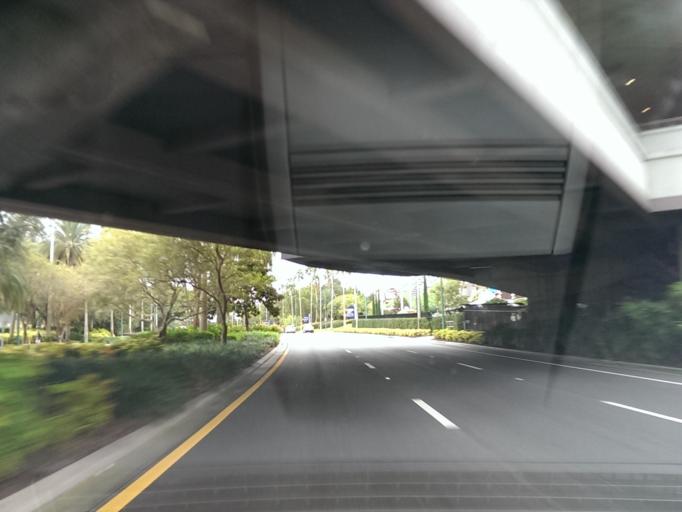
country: US
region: Florida
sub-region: Orange County
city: Tangelo Park
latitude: 28.4741
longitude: -81.4638
